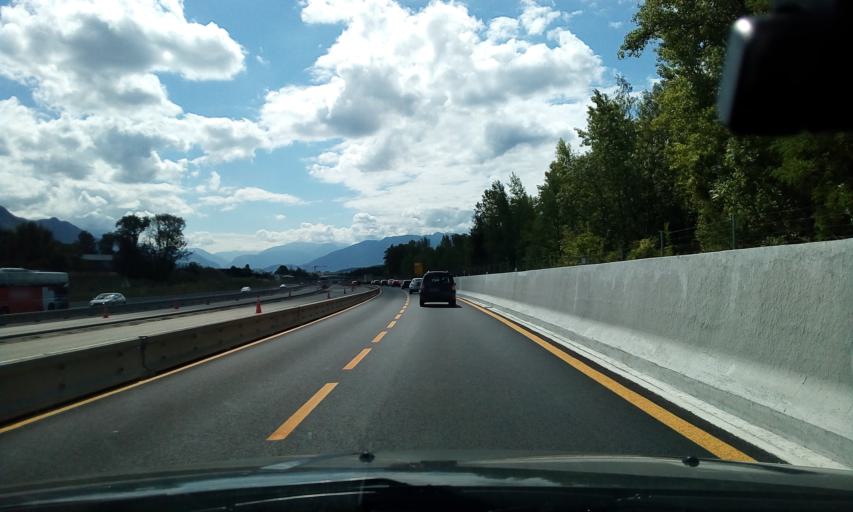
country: FR
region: Rhone-Alpes
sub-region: Departement de la Haute-Savoie
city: Metz-Tessy
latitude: 45.9449
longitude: 6.1118
